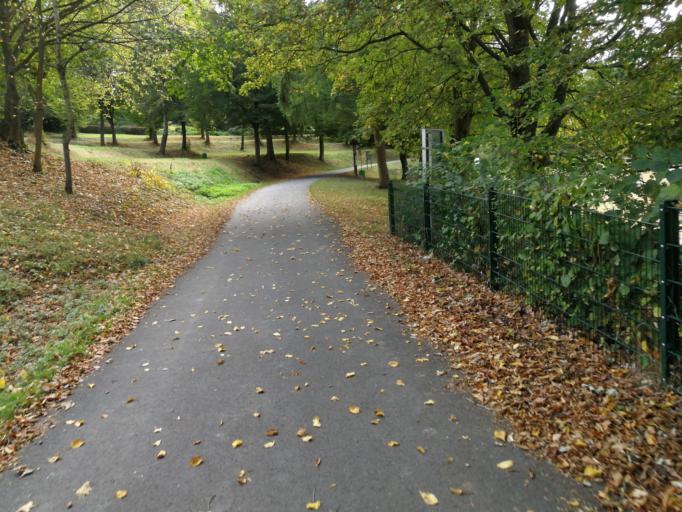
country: DE
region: North Rhine-Westphalia
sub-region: Regierungsbezirk Arnsberg
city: Meschede
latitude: 51.3054
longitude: 8.2621
